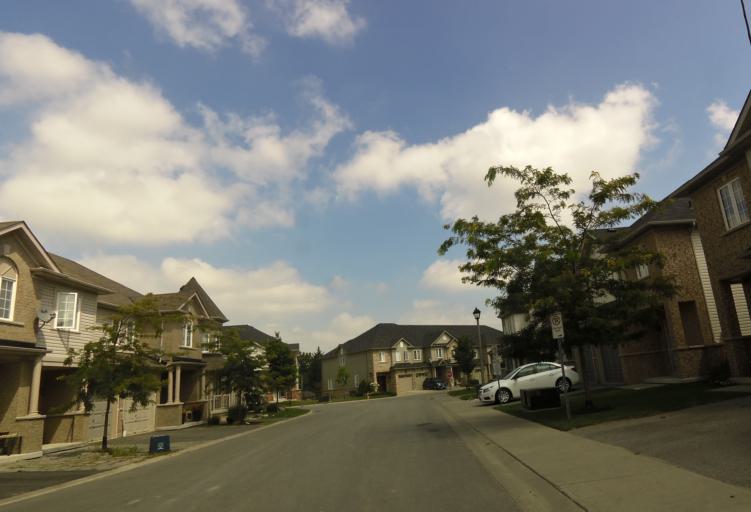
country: CA
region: Ontario
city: Oshawa
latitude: 43.9509
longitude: -78.9587
